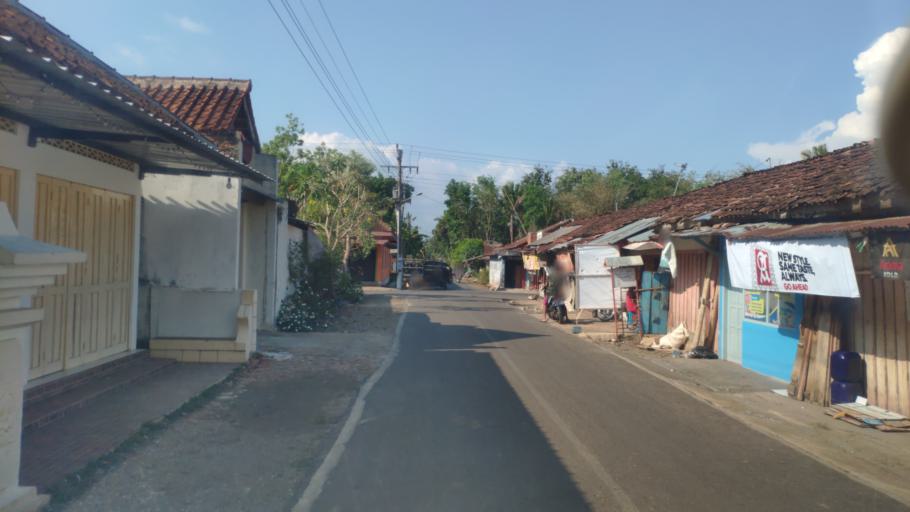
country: ID
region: Central Java
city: Purbalingga
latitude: -7.4778
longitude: 109.4521
